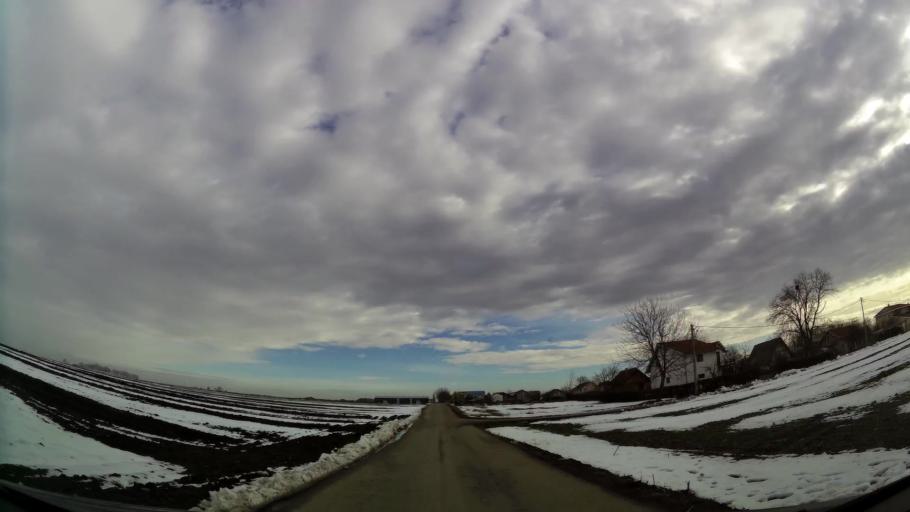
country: RS
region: Central Serbia
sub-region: Belgrade
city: Surcin
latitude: 44.8003
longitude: 20.3068
